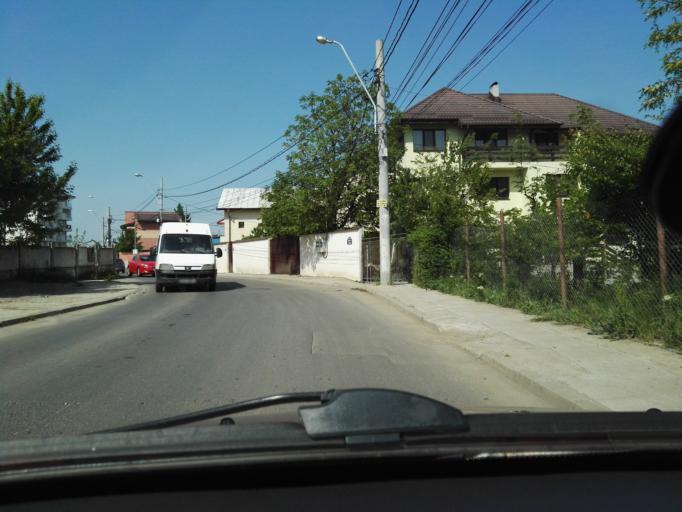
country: RO
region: Ilfov
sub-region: Comuna Popesti-Leordeni
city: Popesti-Leordeni
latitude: 44.3718
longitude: 26.1289
